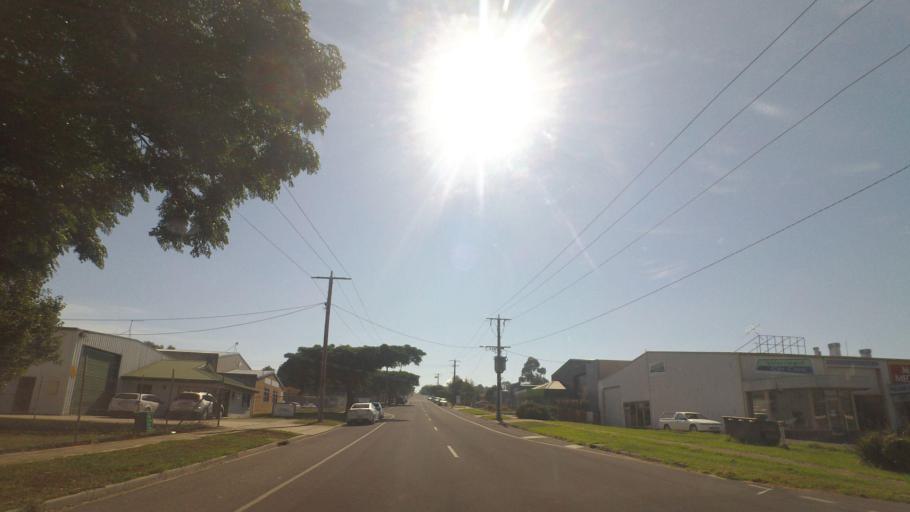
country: AU
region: Victoria
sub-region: Baw Baw
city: Warragul
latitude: -38.1652
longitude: 145.9483
